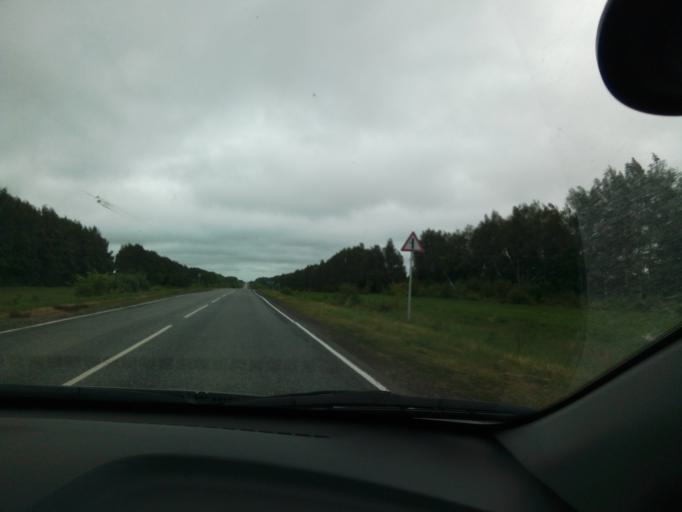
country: RU
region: Chuvashia
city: Alikovo
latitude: 55.6131
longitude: 46.6732
